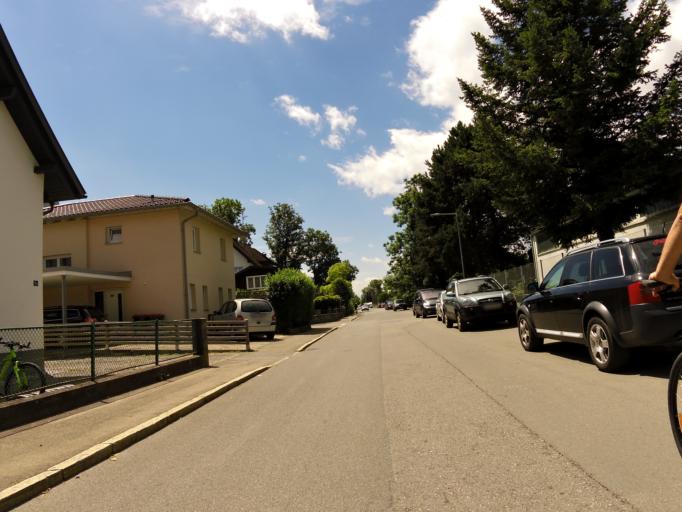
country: AT
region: Vorarlberg
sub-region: Politischer Bezirk Bregenz
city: Hard
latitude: 47.4999
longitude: 9.6916
